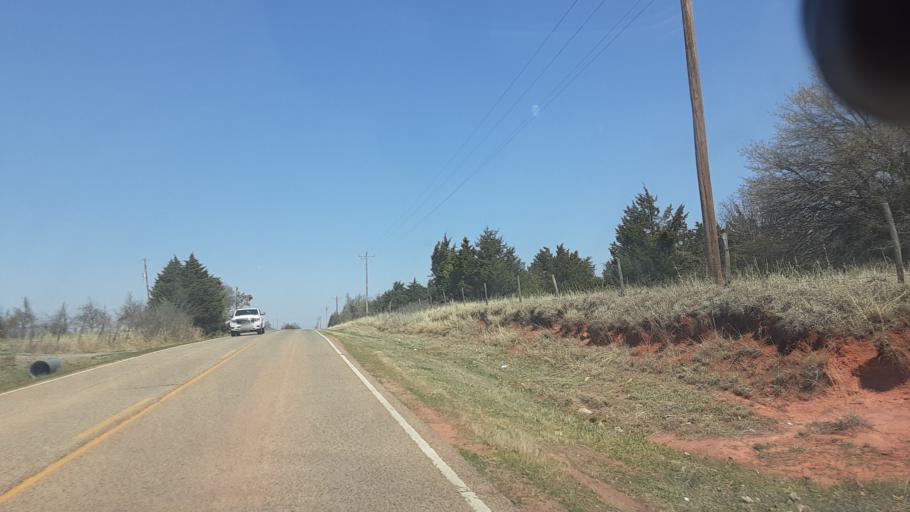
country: US
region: Oklahoma
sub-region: Logan County
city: Guthrie
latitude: 35.8231
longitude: -97.4784
